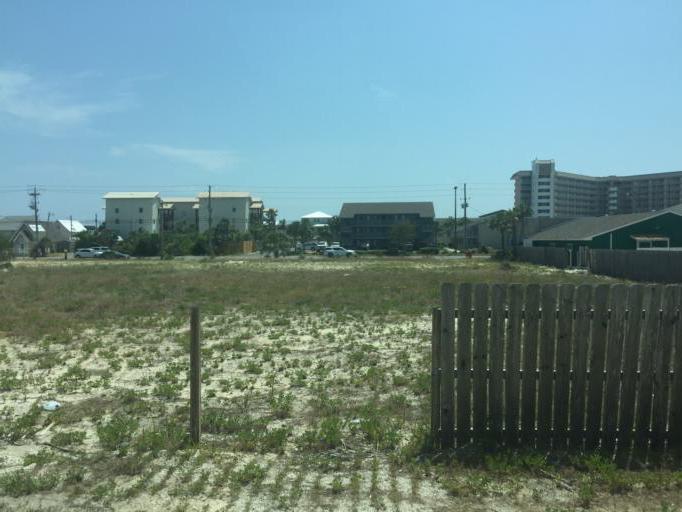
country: US
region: Florida
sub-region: Bay County
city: Lower Grand Lagoon
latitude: 30.1566
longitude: -85.7709
